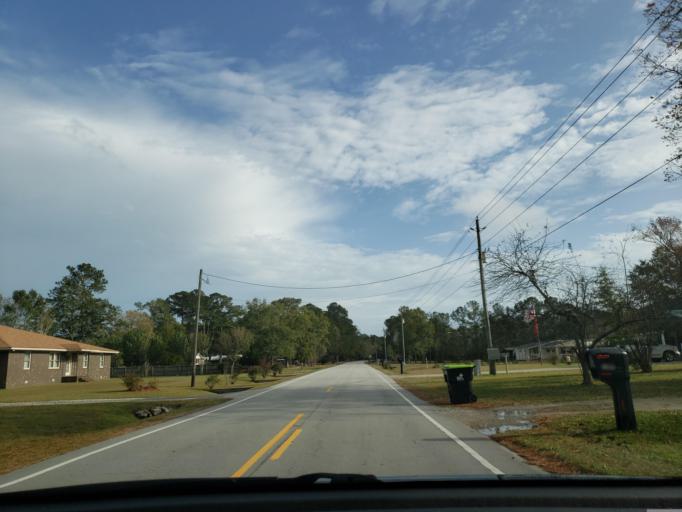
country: US
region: North Carolina
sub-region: Onslow County
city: Jacksonville
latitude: 34.6593
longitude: -77.4807
